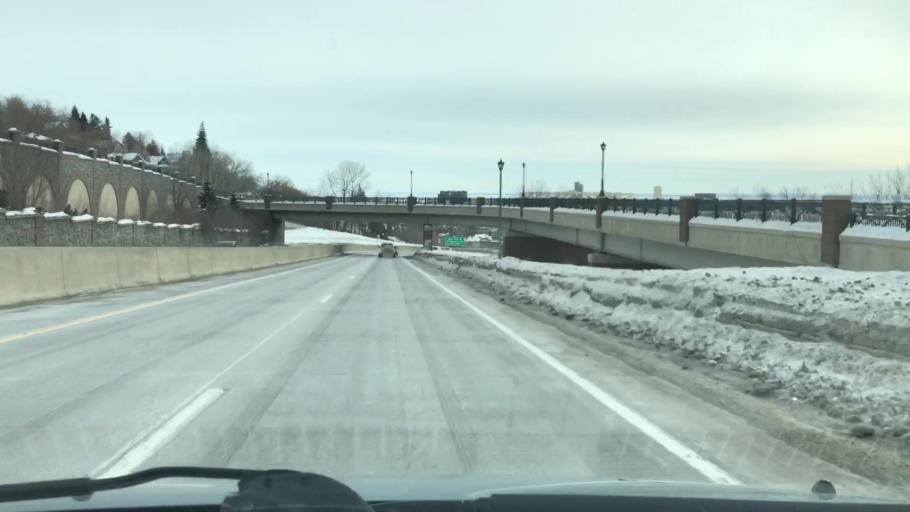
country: US
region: Minnesota
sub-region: Saint Louis County
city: Duluth
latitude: 46.7707
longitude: -92.1288
